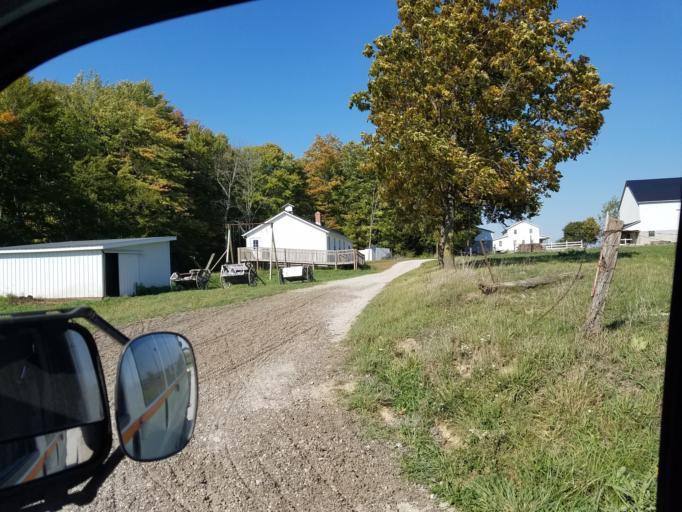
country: US
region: Ohio
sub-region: Ashland County
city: Ashland
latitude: 40.9238
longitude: -82.3719
